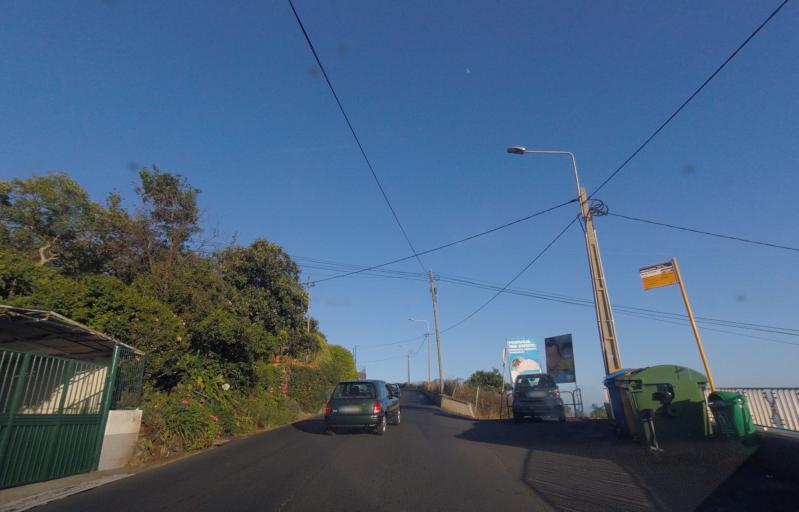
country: PT
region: Madeira
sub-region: Funchal
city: Nossa Senhora do Monte
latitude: 32.6583
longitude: -16.8922
